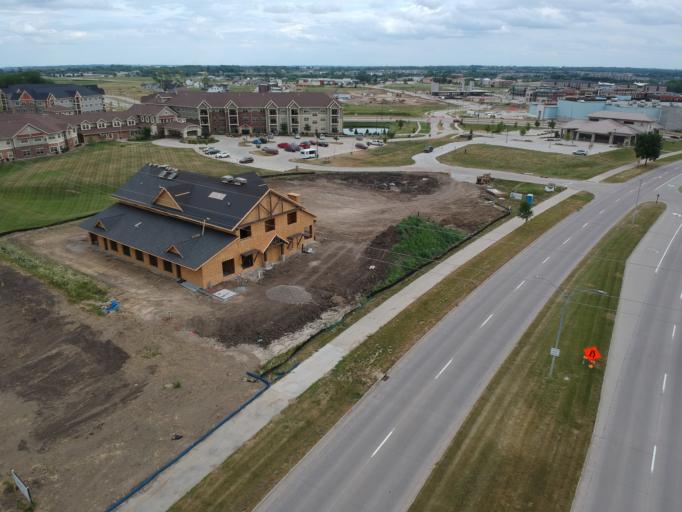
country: US
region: Iowa
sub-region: Polk County
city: Ankeny
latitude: 41.7184
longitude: -93.6198
